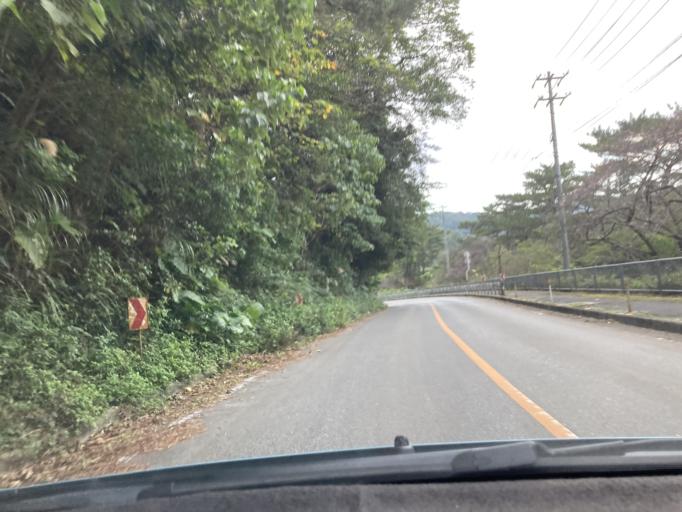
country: JP
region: Okinawa
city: Nago
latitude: 26.8319
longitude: 128.2828
